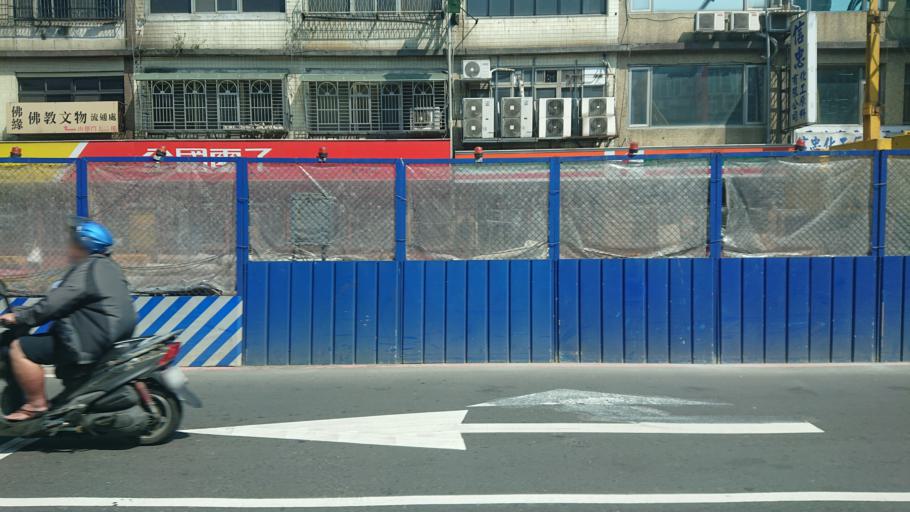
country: TW
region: Taipei
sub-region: Taipei
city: Banqiao
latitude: 25.0262
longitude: 121.5004
